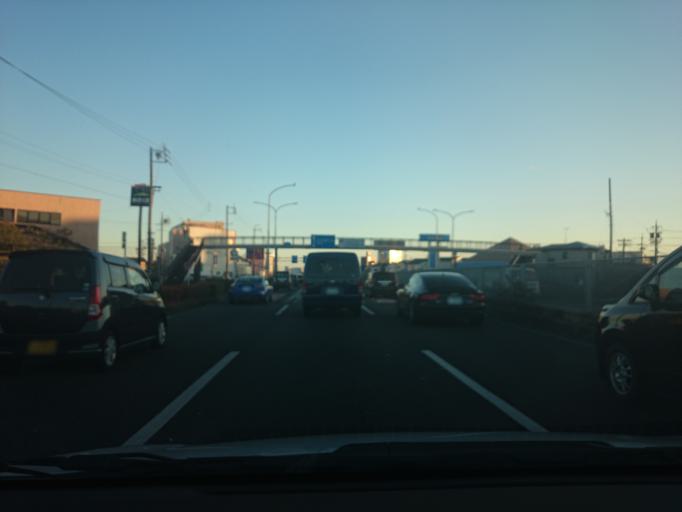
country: JP
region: Aichi
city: Ichinomiya
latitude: 35.3230
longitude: 136.8085
